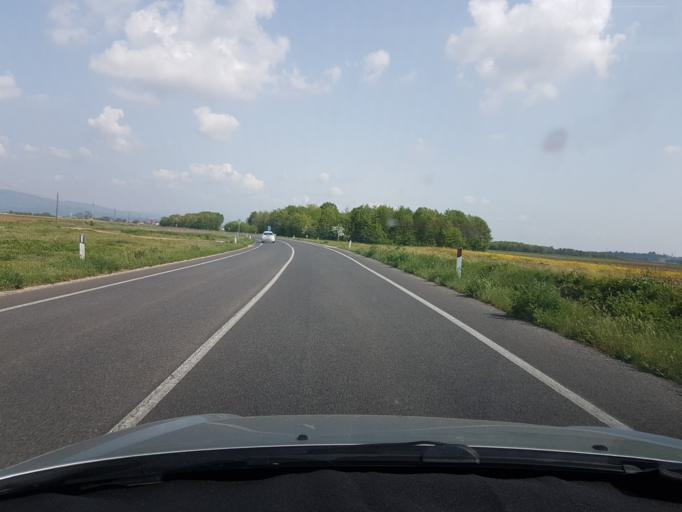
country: IT
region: Friuli Venezia Giulia
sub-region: Provincia di Udine
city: Orsaria
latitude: 46.0383
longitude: 13.3518
